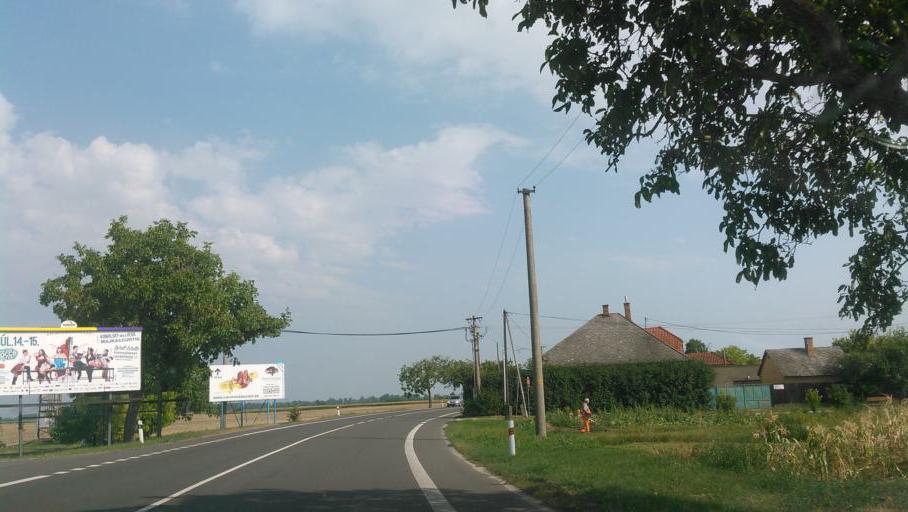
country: SK
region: Trnavsky
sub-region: Okres Dunajska Streda
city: Velky Meder
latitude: 47.9474
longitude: 17.7118
